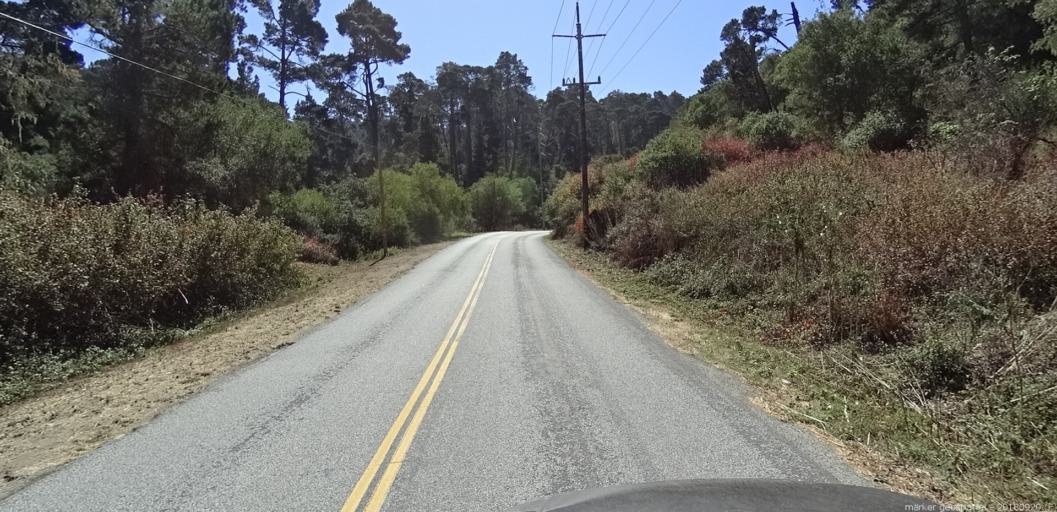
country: US
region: California
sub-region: Monterey County
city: Monterey
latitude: 36.5750
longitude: -121.8741
